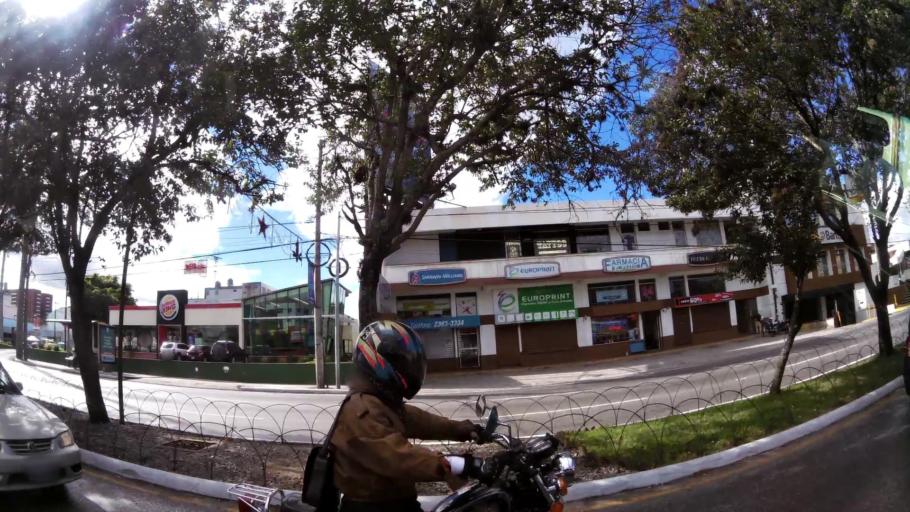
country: GT
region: Guatemala
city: Santa Catarina Pinula
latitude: 14.5911
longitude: -90.5081
